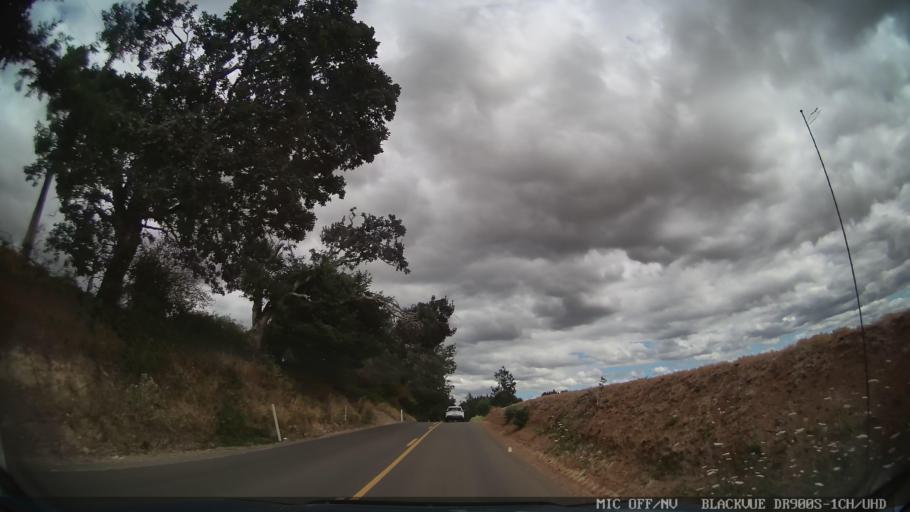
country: US
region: Oregon
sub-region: Marion County
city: Sublimity
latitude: 44.8678
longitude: -122.7517
